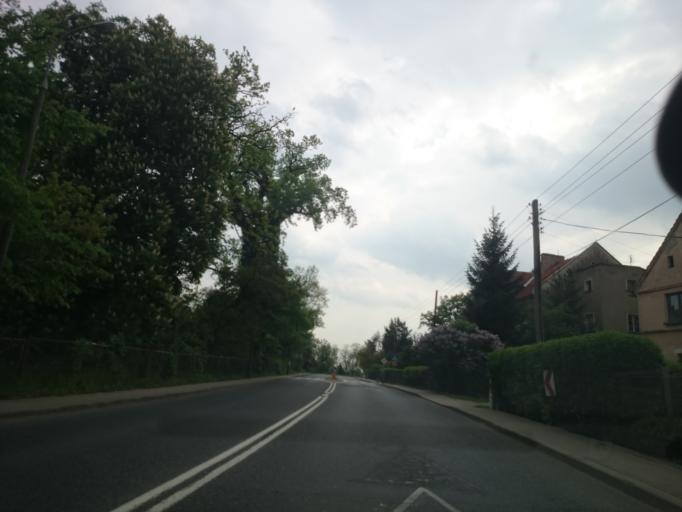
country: PL
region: Lower Silesian Voivodeship
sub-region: Powiat dzierzoniowski
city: Niemcza
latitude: 50.7502
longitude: 16.8460
